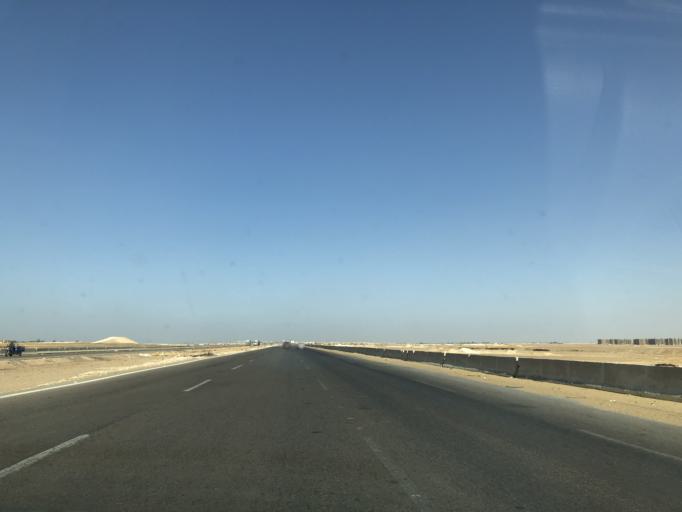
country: EG
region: Muhafazat al Minufiyah
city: Ashmun
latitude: 30.0675
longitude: 30.8790
